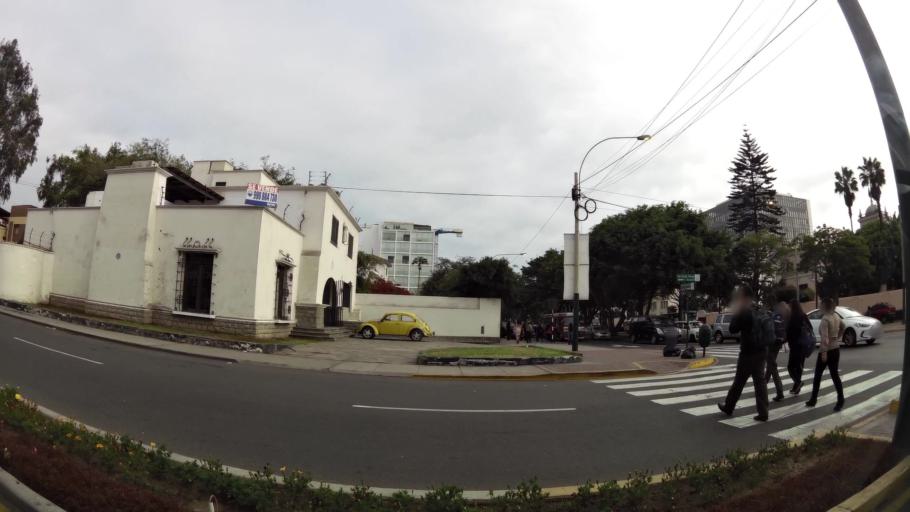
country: PE
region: Lima
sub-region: Lima
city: San Isidro
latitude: -12.1013
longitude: -77.0573
